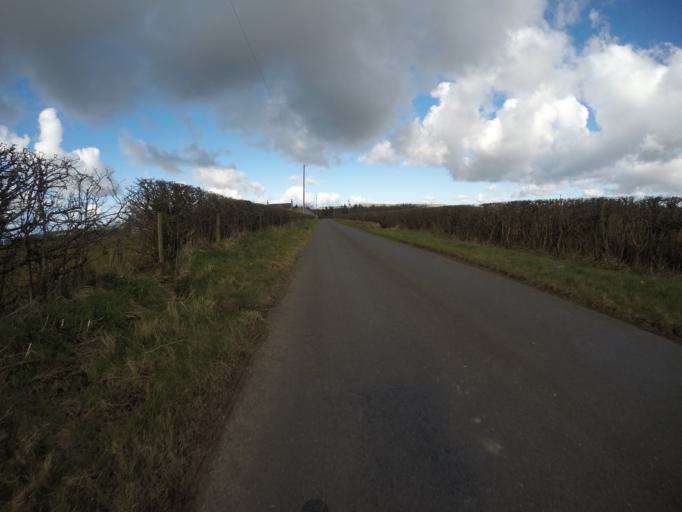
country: GB
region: Scotland
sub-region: North Ayrshire
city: Kilwinning
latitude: 55.6898
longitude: -4.6685
